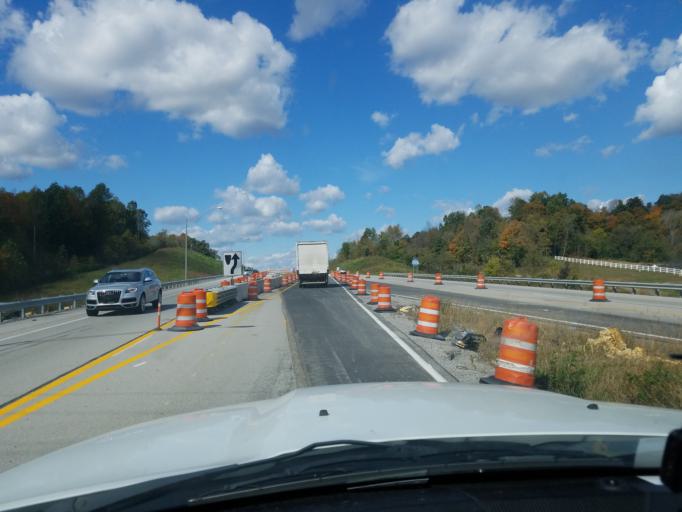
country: US
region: Kentucky
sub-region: Ohio County
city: Hartford
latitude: 37.4591
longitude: -86.8837
